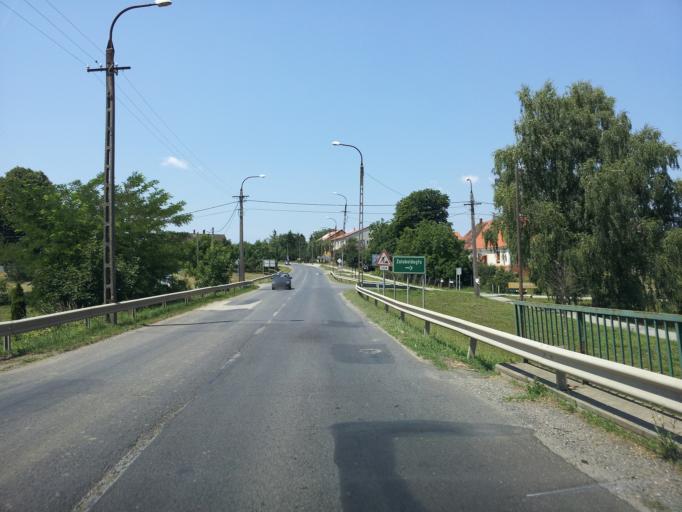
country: HU
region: Zala
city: Zalaegerszeg
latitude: 46.8763
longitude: 16.7524
